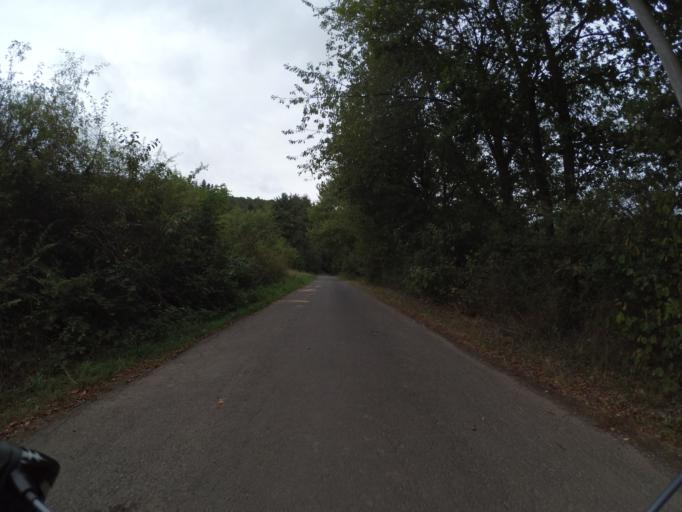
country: DE
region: Rheinland-Pfalz
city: Bekond
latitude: 49.8360
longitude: 6.8126
